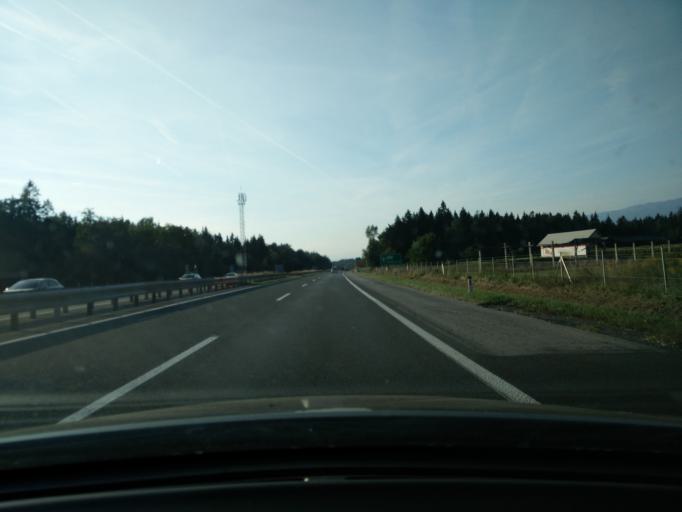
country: SI
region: Sencur
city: Sencur
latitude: 46.2346
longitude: 14.4082
